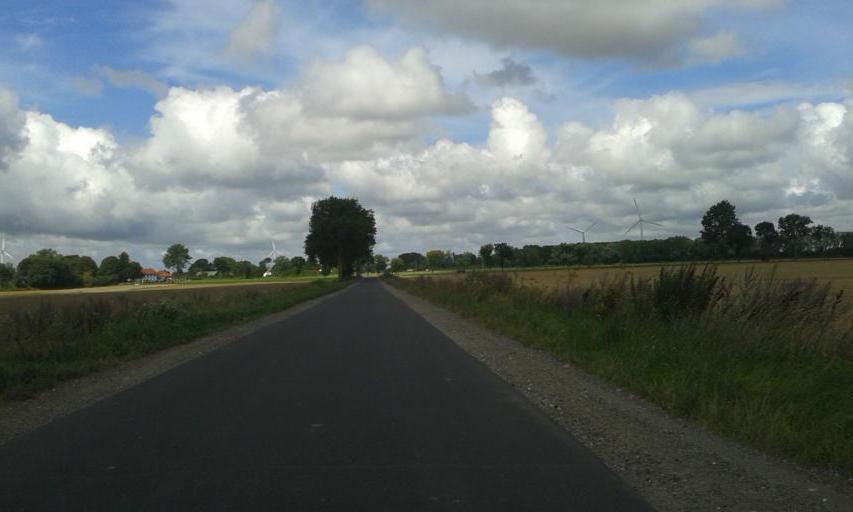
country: PL
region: West Pomeranian Voivodeship
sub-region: Powiat slawienski
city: Slawno
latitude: 54.3265
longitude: 16.5753
